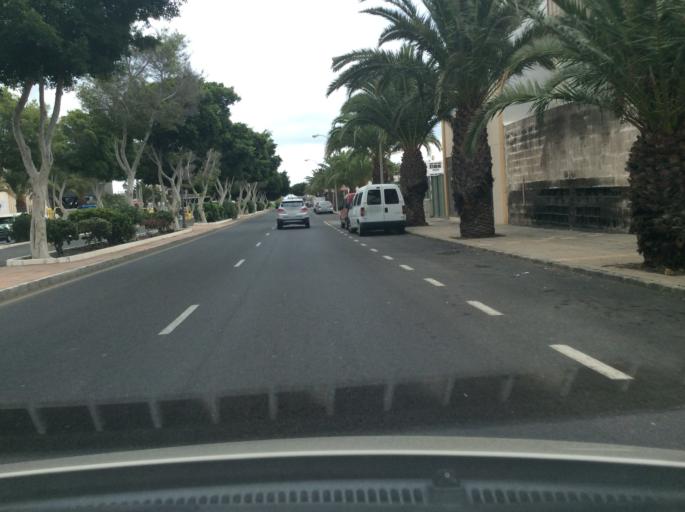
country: ES
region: Canary Islands
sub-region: Provincia de Las Palmas
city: Arrecife
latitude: 28.9685
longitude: -13.5459
